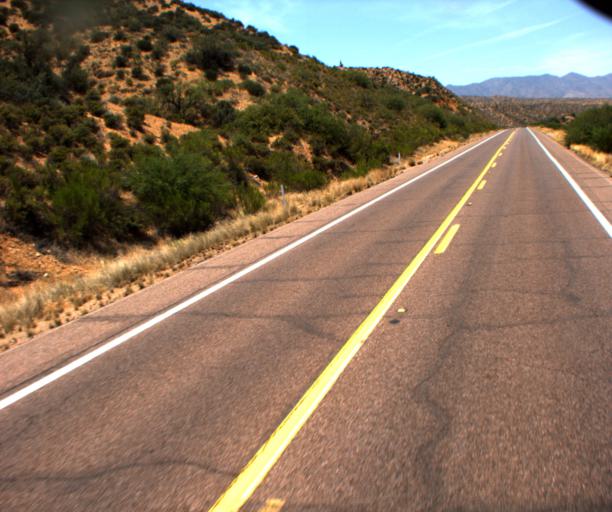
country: US
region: Arizona
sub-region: Gila County
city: Tonto Basin
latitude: 33.7531
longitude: -111.2420
